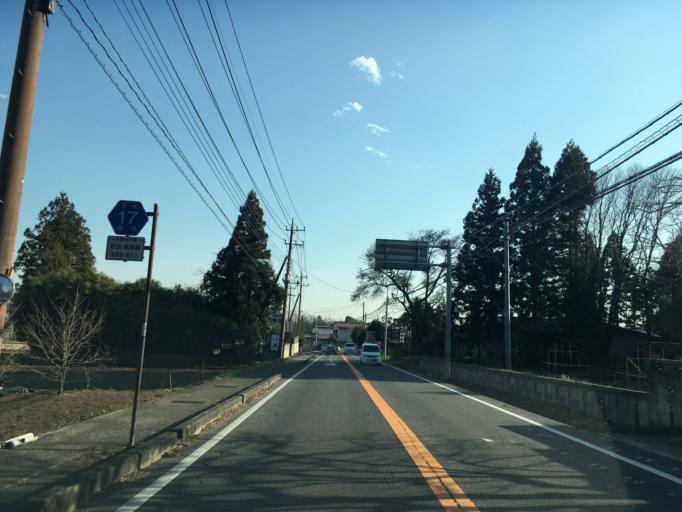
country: JP
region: Tochigi
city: Kuroiso
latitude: 37.0460
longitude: 140.0133
